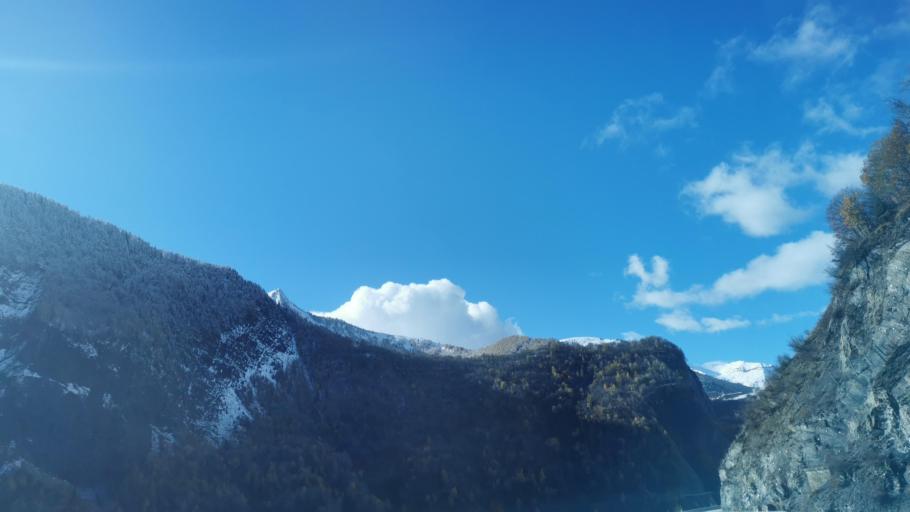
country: FR
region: Rhone-Alpes
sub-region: Departement de l'Isere
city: Mont-de-Lans
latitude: 45.0450
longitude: 6.1563
